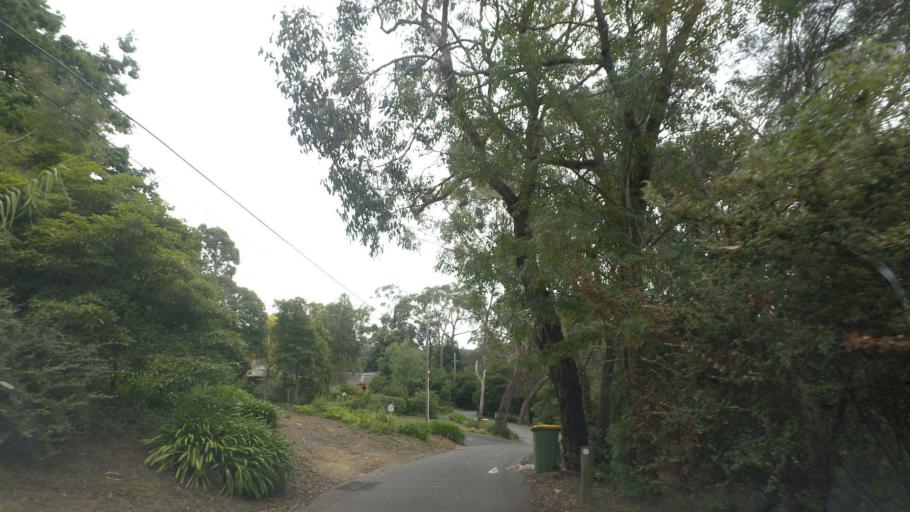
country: AU
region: Victoria
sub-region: Yarra Ranges
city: Kilsyth
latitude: -37.7917
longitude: 145.3366
